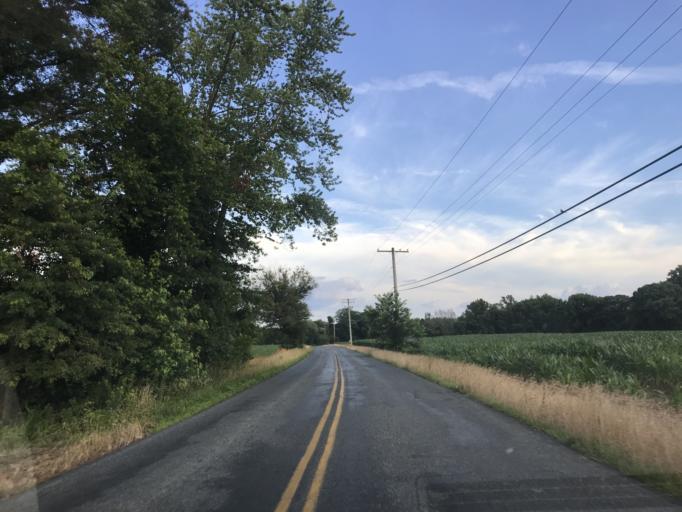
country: US
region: Maryland
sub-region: Harford County
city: Riverside
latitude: 39.5359
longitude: -76.2248
